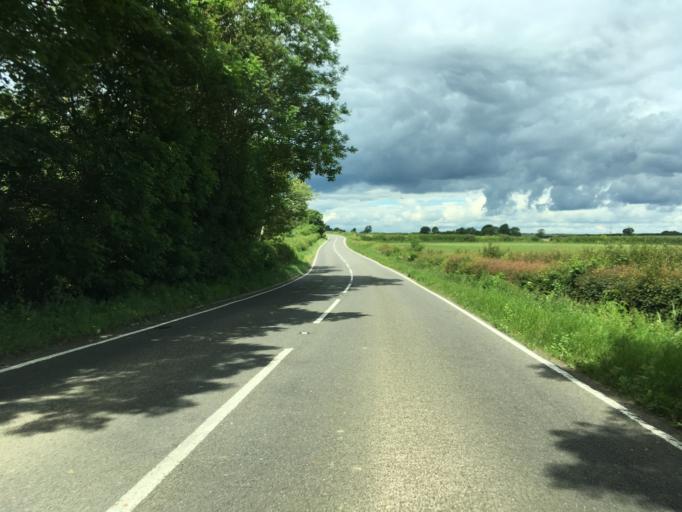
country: GB
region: England
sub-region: Northamptonshire
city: Brackley
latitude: 52.0879
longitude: -1.1940
